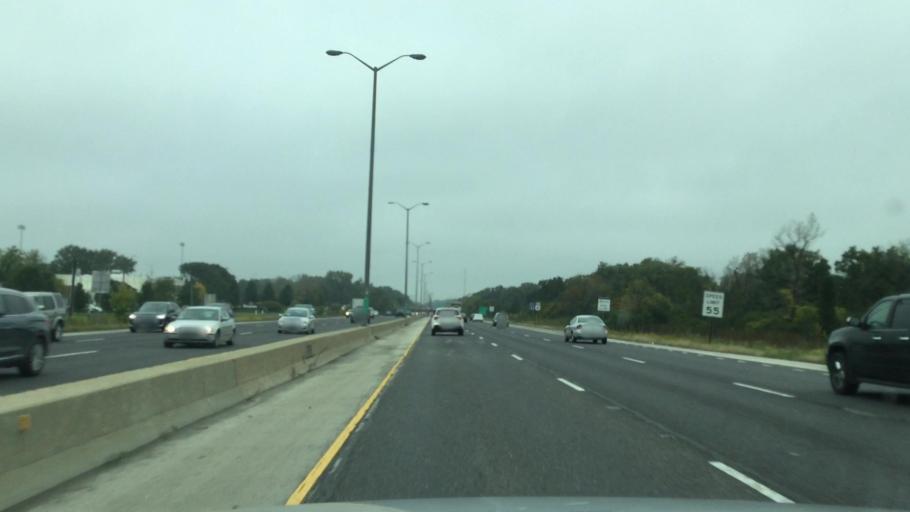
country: US
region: Illinois
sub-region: Cook County
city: Northfield
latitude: 42.0894
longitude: -87.7598
